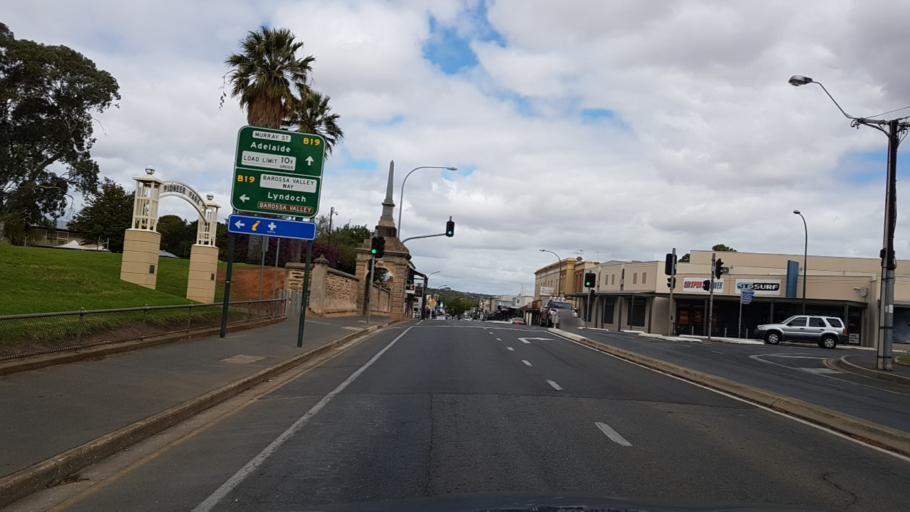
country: AU
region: South Australia
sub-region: Gawler
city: Gawler
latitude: -34.5957
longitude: 138.7491
